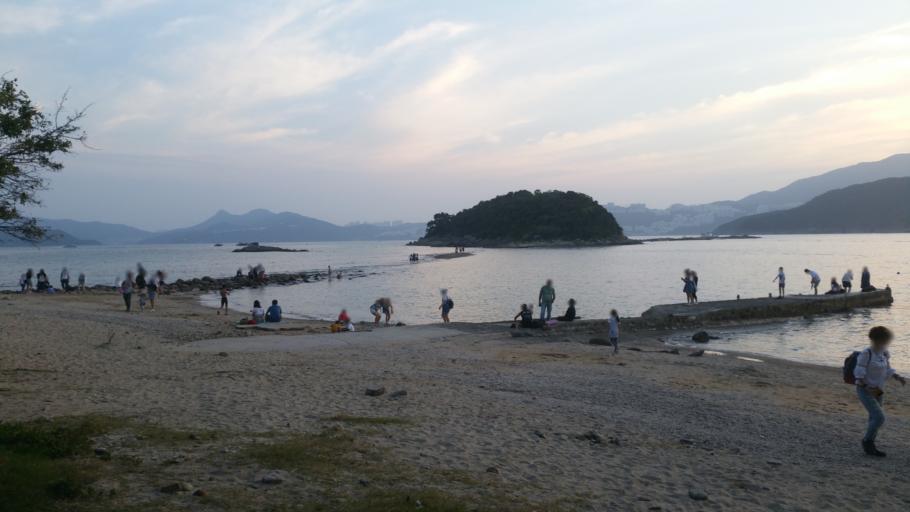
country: HK
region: Sai Kung
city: Sai Kung
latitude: 22.3667
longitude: 114.2884
